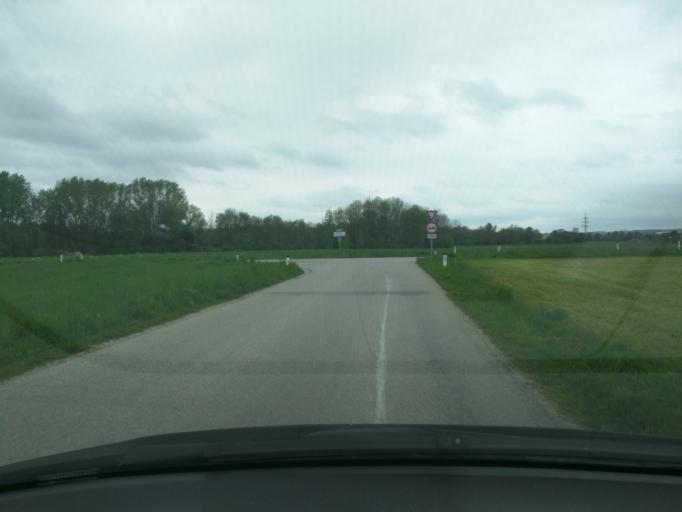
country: AT
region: Lower Austria
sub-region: Politischer Bezirk Amstetten
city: Euratsfeld
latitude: 48.1060
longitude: 14.9432
